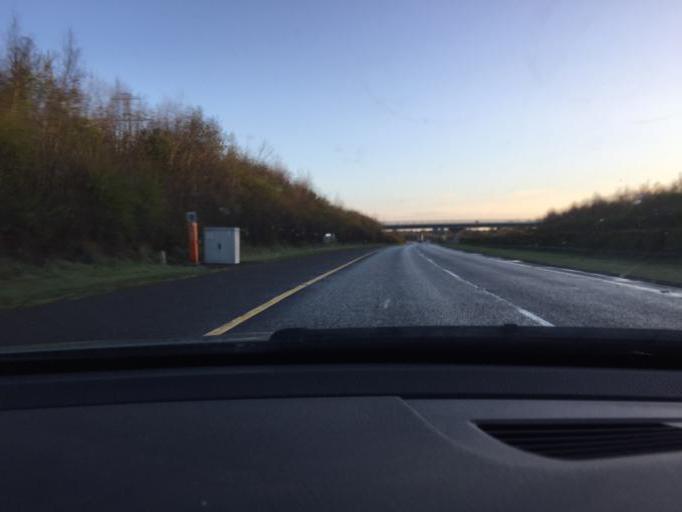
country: IE
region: Leinster
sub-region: Fingal County
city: Swords
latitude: 53.4897
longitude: -6.2051
